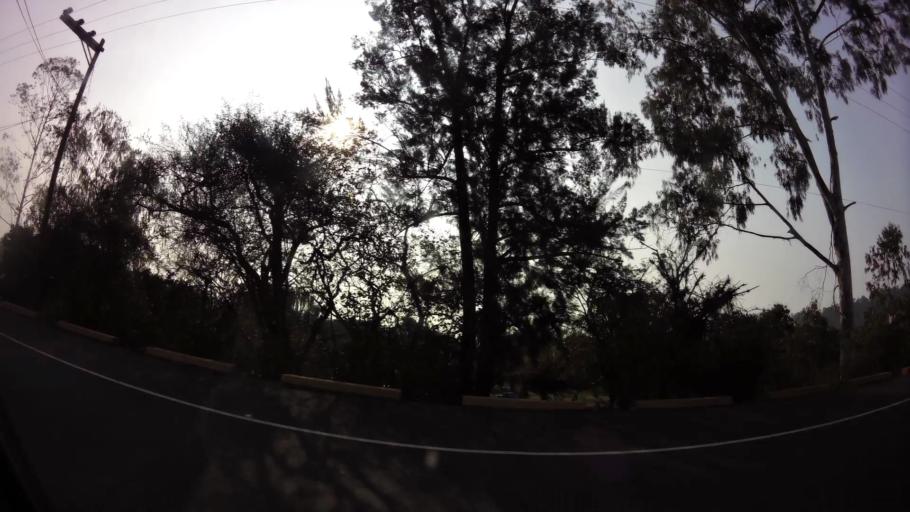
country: HN
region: Francisco Morazan
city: Zambrano
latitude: 14.2818
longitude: -87.4033
